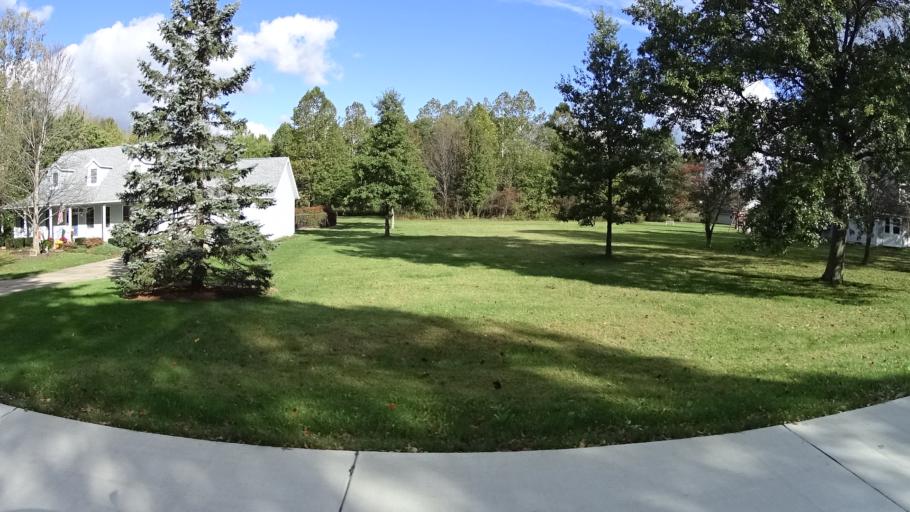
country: US
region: Ohio
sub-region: Lorain County
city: Grafton
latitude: 41.2962
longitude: -82.0715
